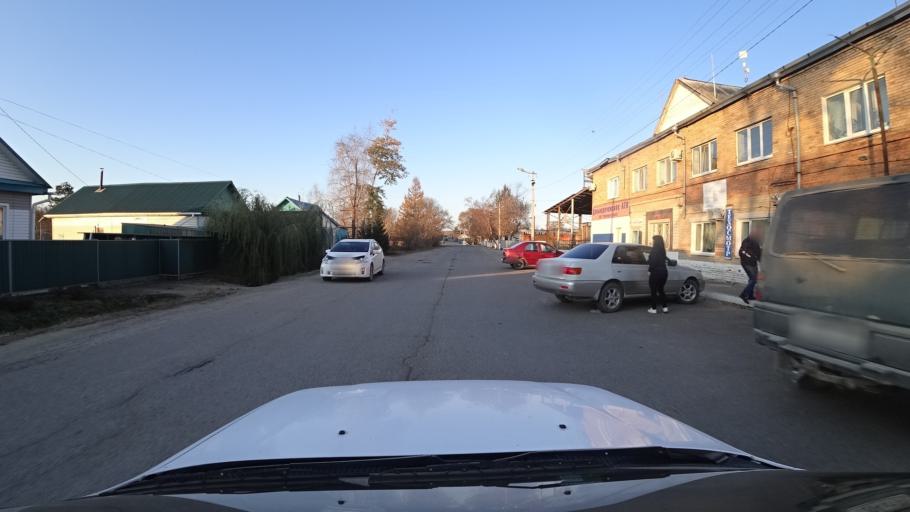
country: RU
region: Primorskiy
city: Dal'nerechensk
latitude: 45.9247
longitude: 133.7310
